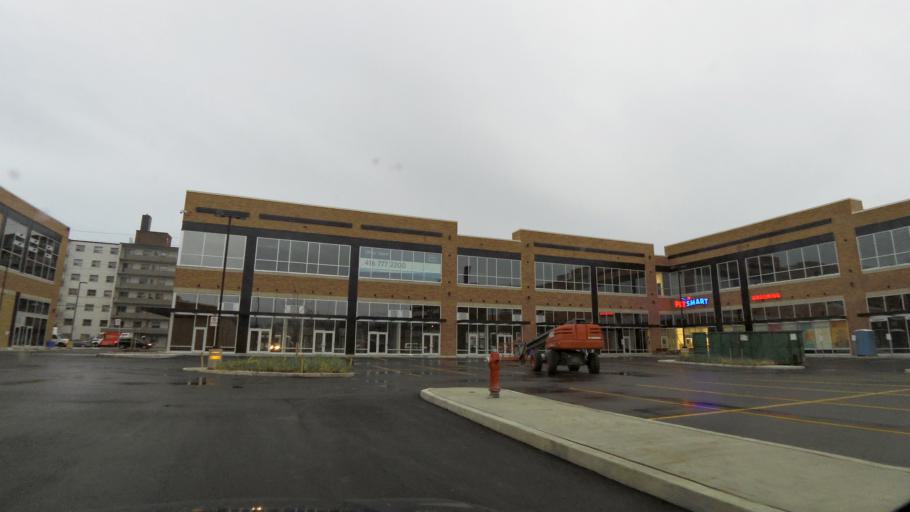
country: CA
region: Ontario
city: Mississauga
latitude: 43.5661
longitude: -79.5716
